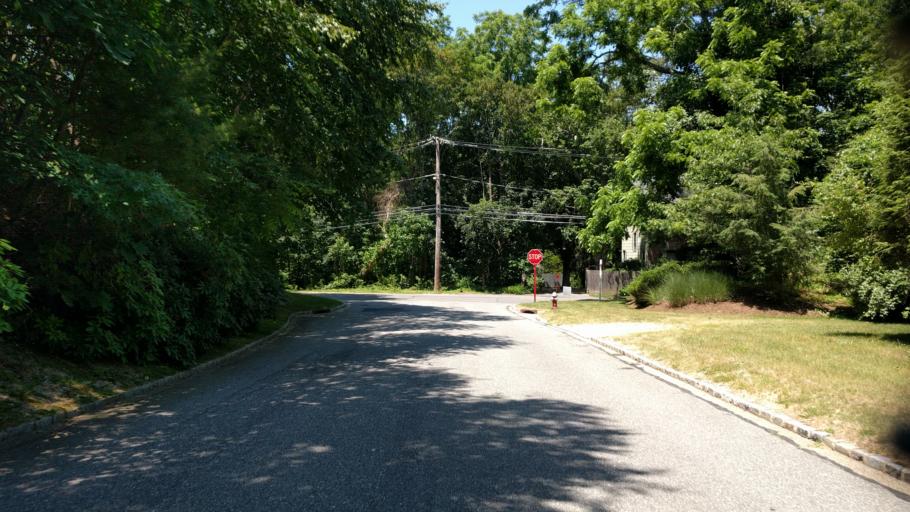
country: US
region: New York
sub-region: Nassau County
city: Oyster Bay
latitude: 40.8637
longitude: -73.5422
